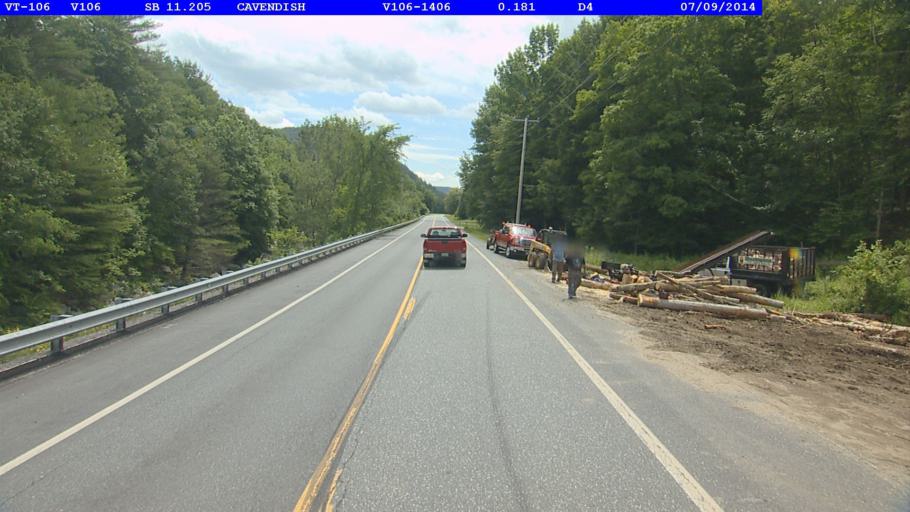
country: US
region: Vermont
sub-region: Windsor County
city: Springfield
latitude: 43.4407
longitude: -72.5334
